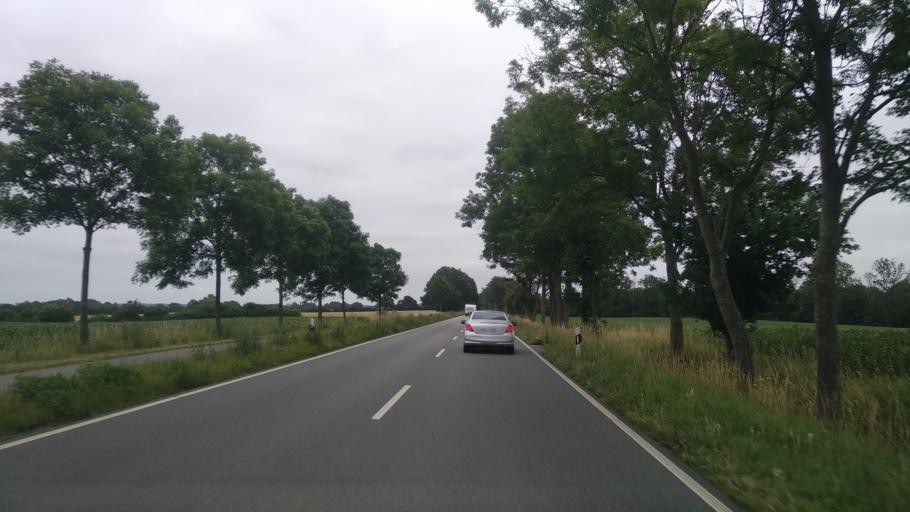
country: DE
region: Schleswig-Holstein
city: Langballig
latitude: 54.8017
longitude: 9.6160
